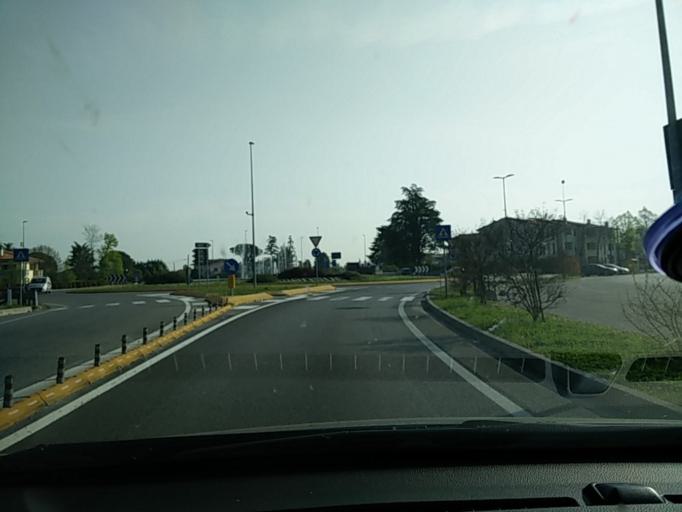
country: IT
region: Veneto
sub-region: Provincia di Treviso
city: Mansue
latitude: 45.8206
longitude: 12.5297
